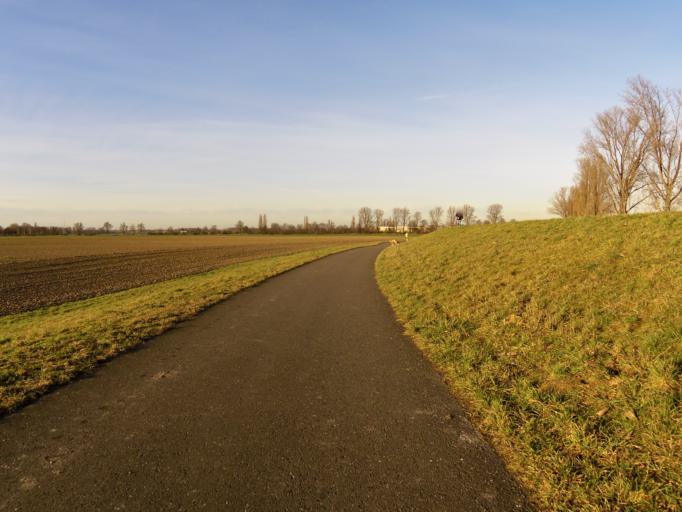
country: DE
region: Rheinland-Pfalz
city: Bobenheim-Roxheim
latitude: 49.5624
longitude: 8.4119
